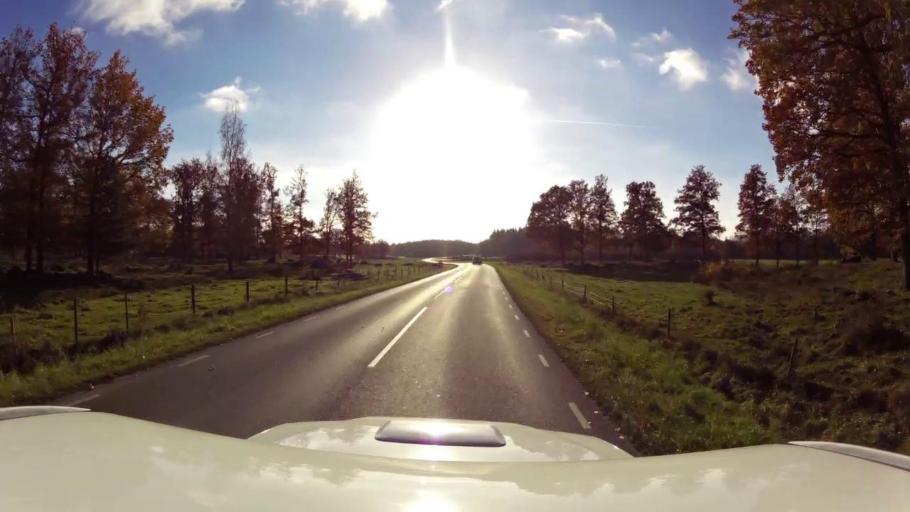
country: SE
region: OEstergoetland
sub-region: Linkopings Kommun
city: Malmslatt
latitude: 58.3327
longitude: 15.5129
